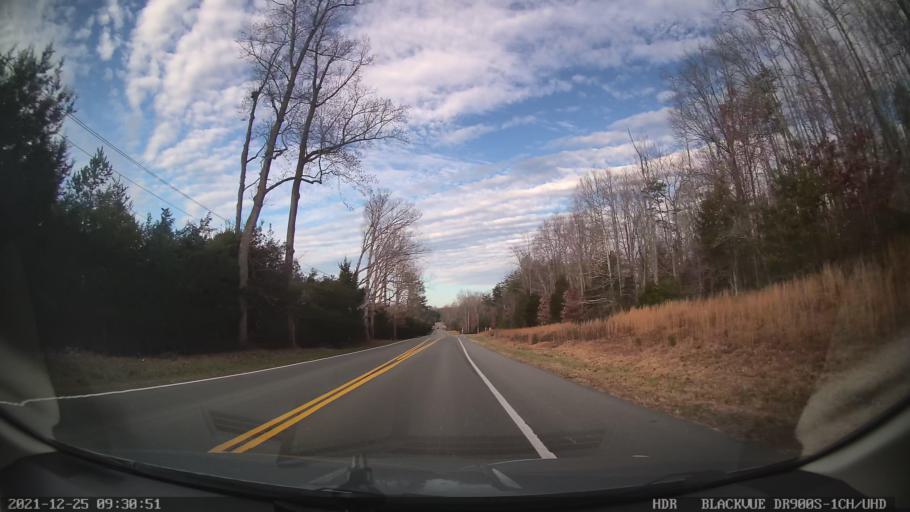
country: US
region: Virginia
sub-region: Goochland County
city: Goochland
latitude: 37.7120
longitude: -77.8116
